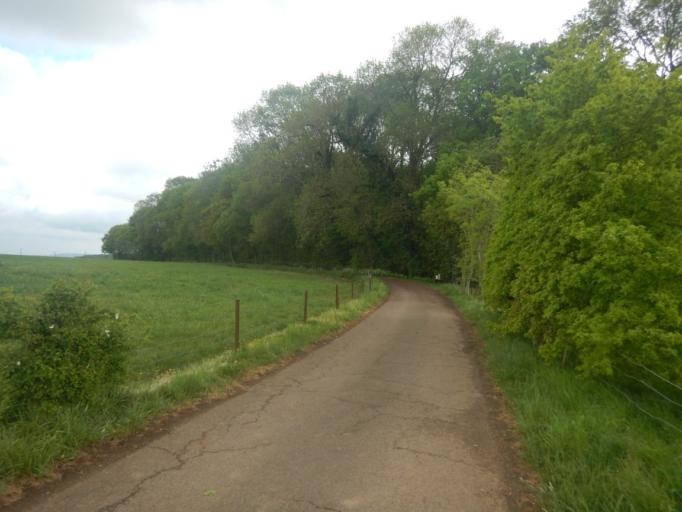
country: LU
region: Luxembourg
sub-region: Canton d'Esch-sur-Alzette
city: Reckange-sur-Mess
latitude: 49.5573
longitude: 5.9984
